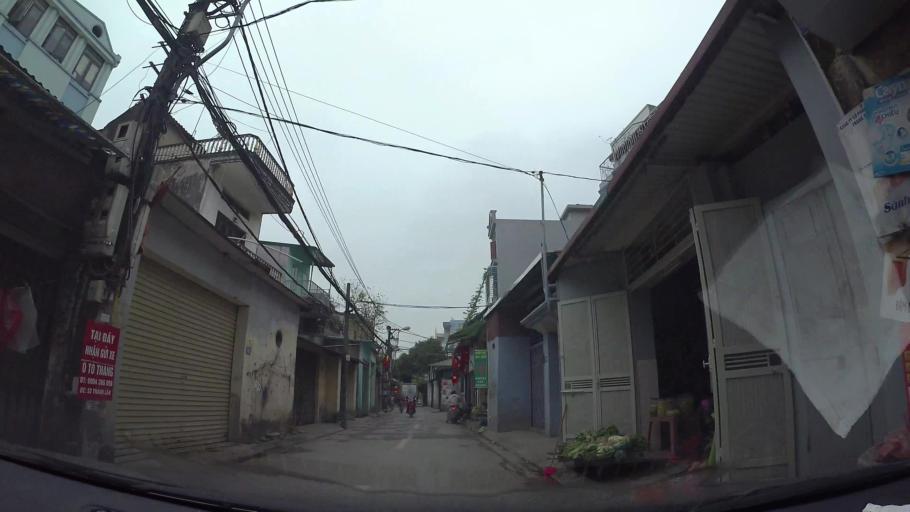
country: VN
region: Ha Noi
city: Hai BaTrung
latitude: 20.9916
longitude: 105.8887
